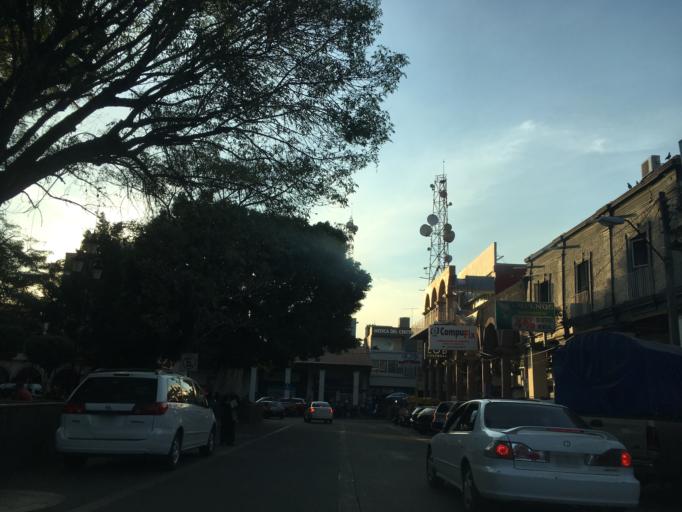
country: MX
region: Michoacan
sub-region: Los Reyes
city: La Higuerita (Colonia San Rafael)
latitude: 19.5897
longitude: -102.4738
